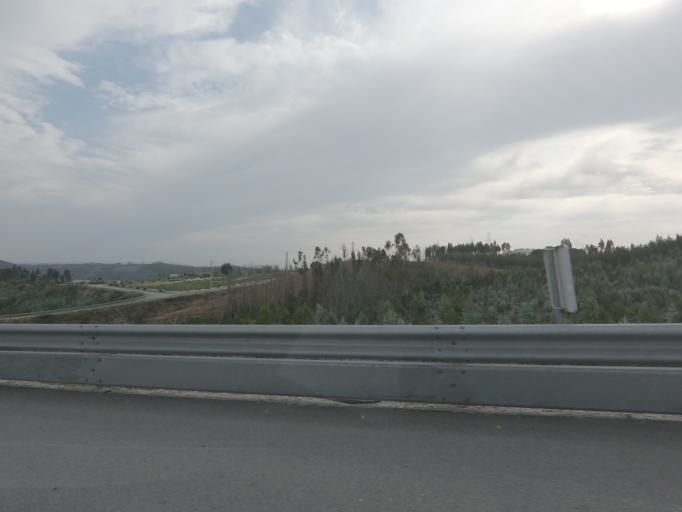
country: PT
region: Viseu
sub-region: Mortagua
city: Mortagua
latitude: 40.3498
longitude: -8.1875
